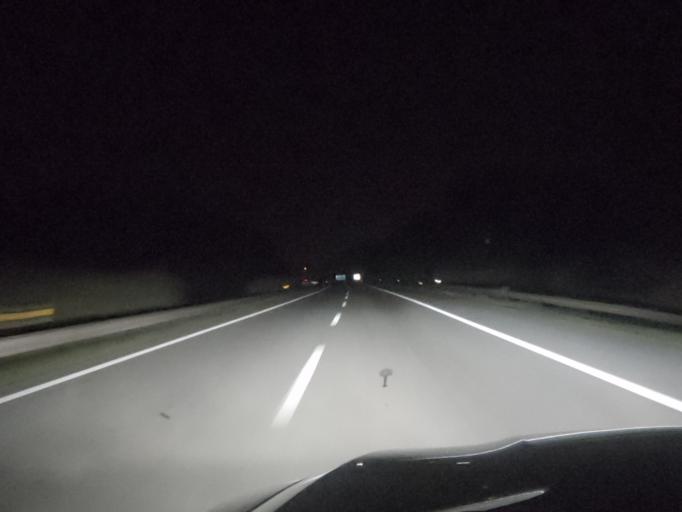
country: PT
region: Aveiro
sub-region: Estarreja
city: Salreu
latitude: 40.7349
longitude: -8.5236
